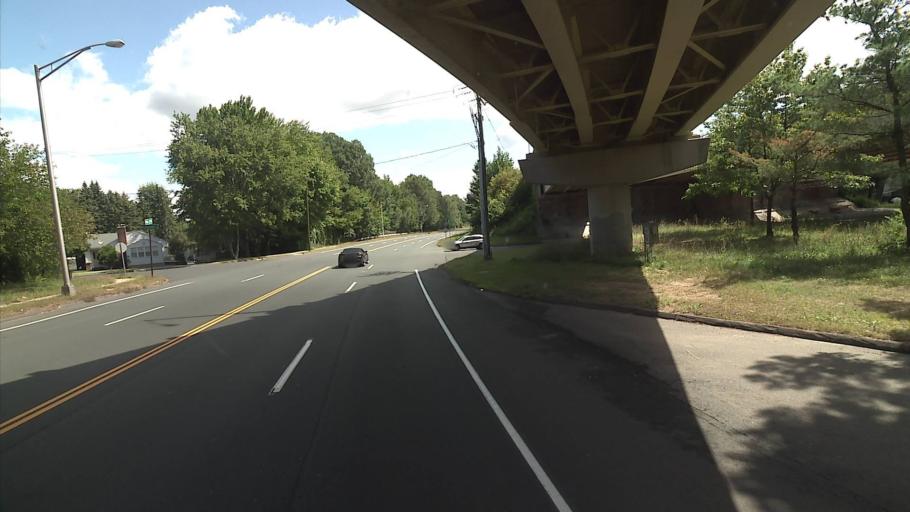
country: US
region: Connecticut
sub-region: Hartford County
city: Blue Hills
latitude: 41.8195
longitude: -72.6631
